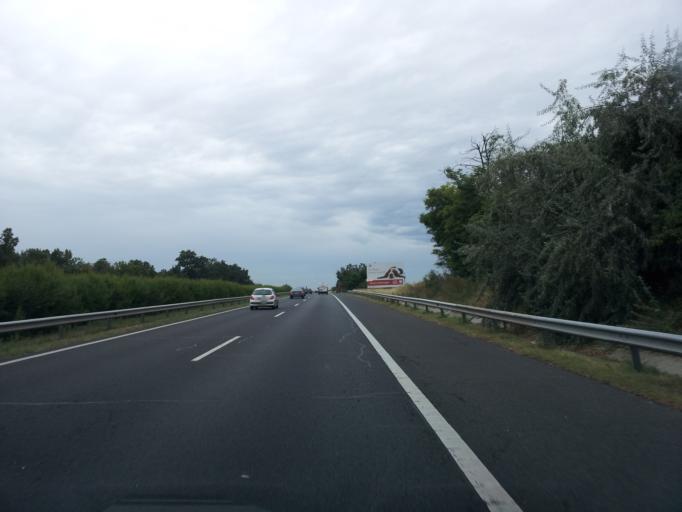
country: HU
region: Fejer
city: Martonvasar
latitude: 47.3517
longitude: 18.8018
